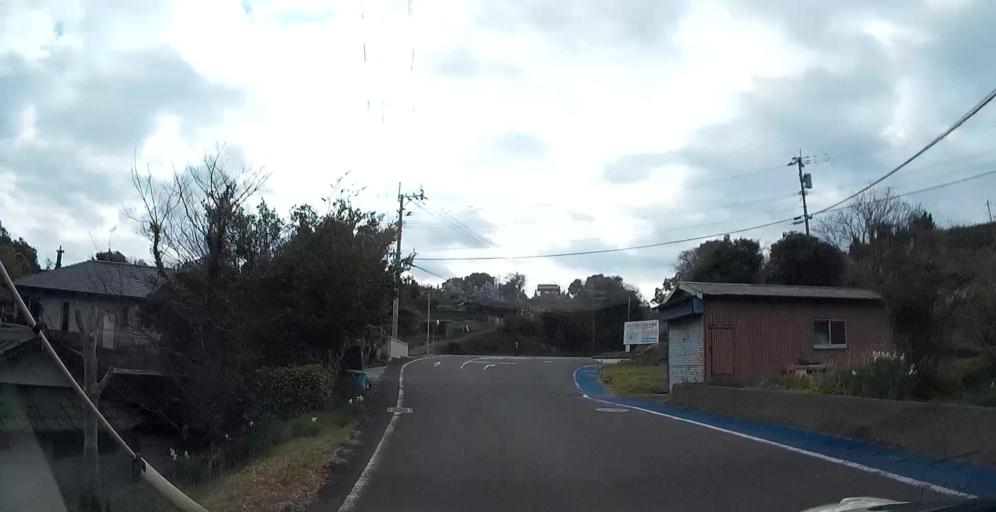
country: JP
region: Kumamoto
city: Minamata
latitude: 32.2112
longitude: 130.3854
